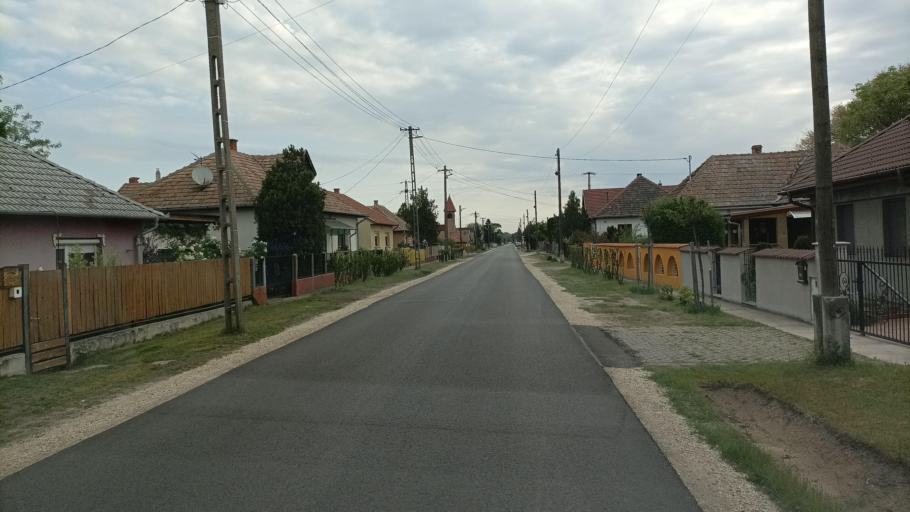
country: HU
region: Pest
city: Monor
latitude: 47.2923
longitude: 19.4238
